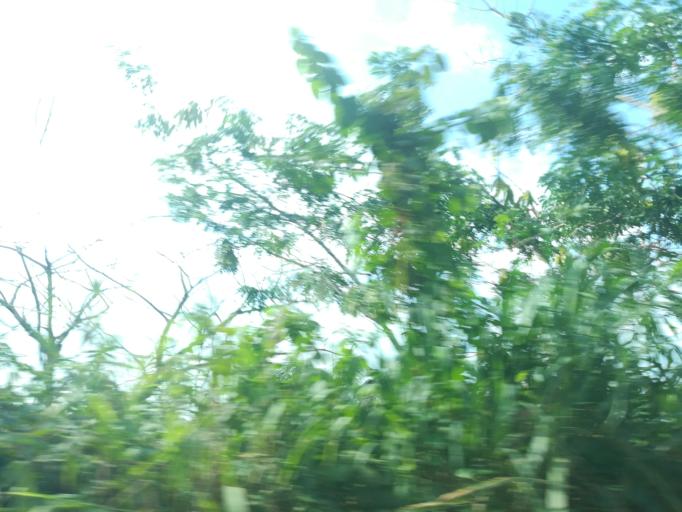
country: NG
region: Lagos
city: Ikorodu
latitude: 6.6309
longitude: 3.5254
